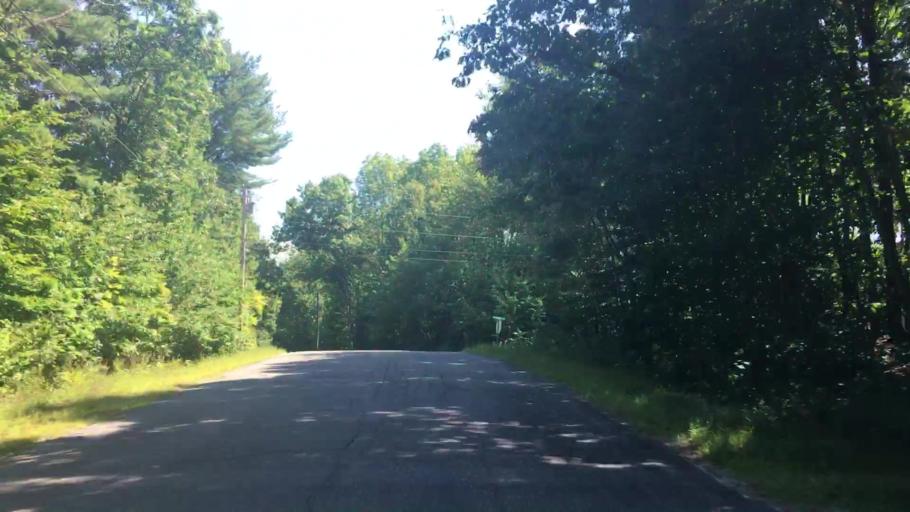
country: US
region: Maine
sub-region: Androscoggin County
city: Sabattus
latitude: 44.1187
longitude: -70.0319
